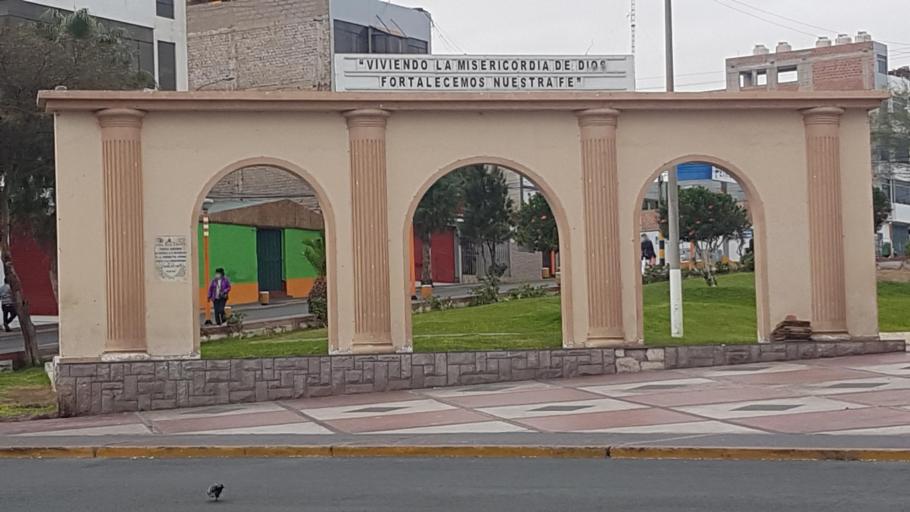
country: PE
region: Moquegua
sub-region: Provincia de Ilo
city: Ilo
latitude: -17.6460
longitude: -71.3452
